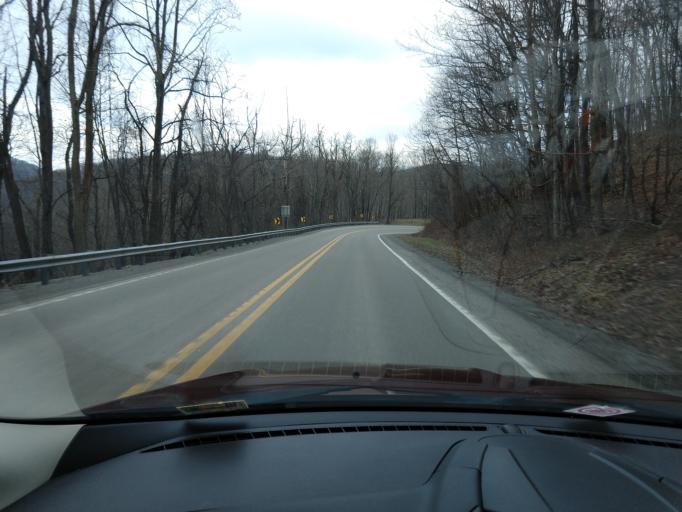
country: US
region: West Virginia
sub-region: Randolph County
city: Elkins
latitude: 38.6582
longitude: -79.9237
